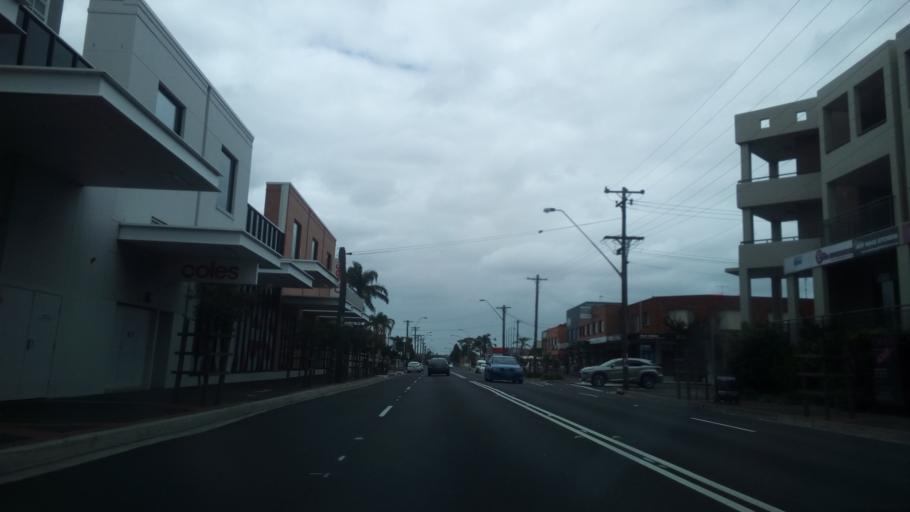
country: AU
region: New South Wales
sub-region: Wollongong
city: Fairy Meadow
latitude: -34.3943
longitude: 150.8929
